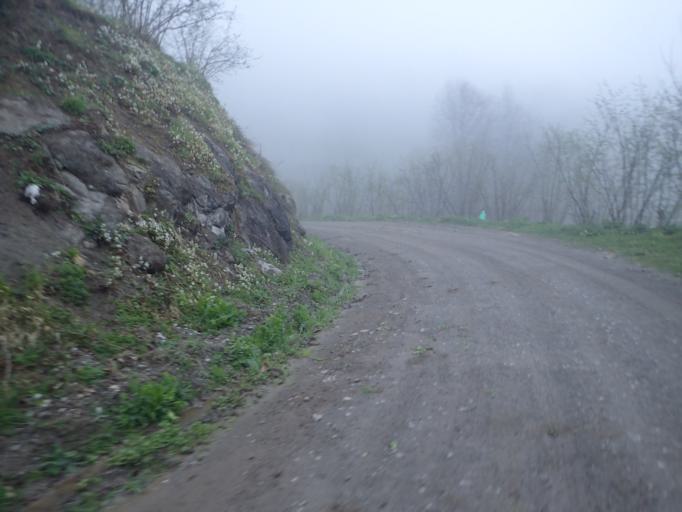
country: TR
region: Ordu
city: Korgan
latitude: 40.7789
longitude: 37.2978
